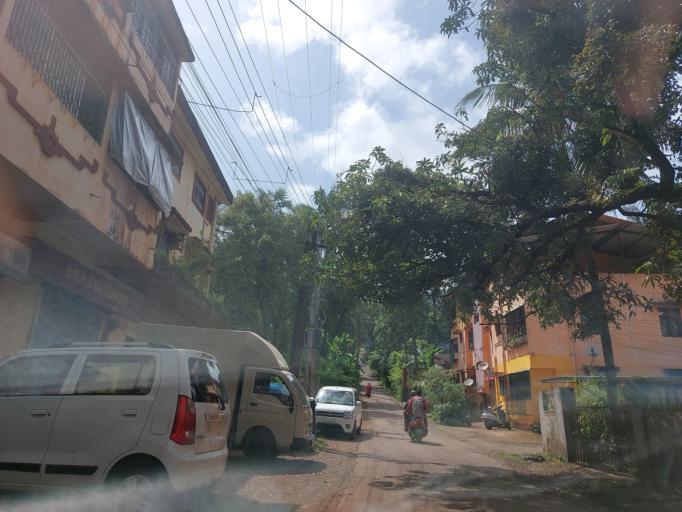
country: IN
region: Goa
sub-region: North Goa
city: Queula
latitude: 15.3983
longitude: 73.9993
